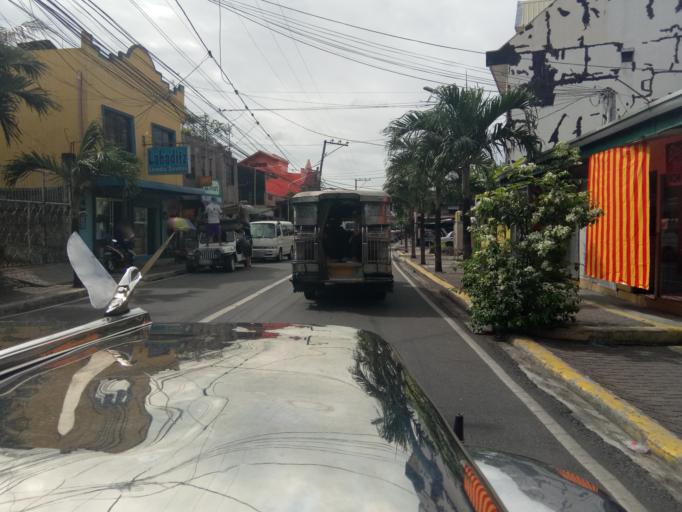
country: PH
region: Calabarzon
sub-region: Province of Cavite
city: Dasmarinas
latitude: 14.3179
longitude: 120.9423
